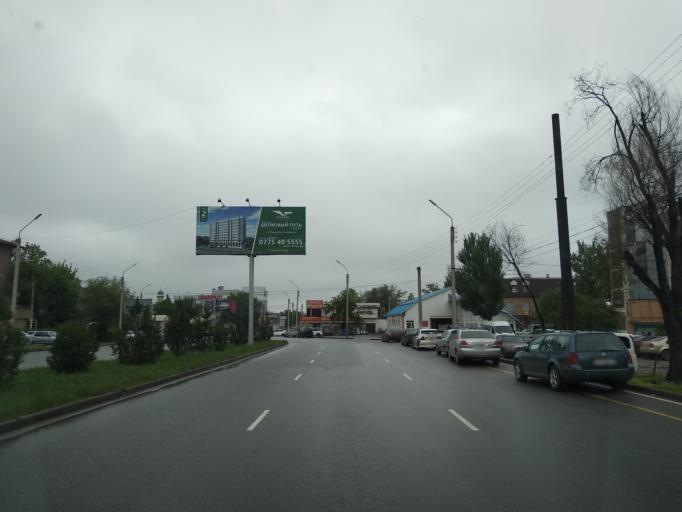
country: KG
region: Chuy
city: Bishkek
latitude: 42.8831
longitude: 74.6174
